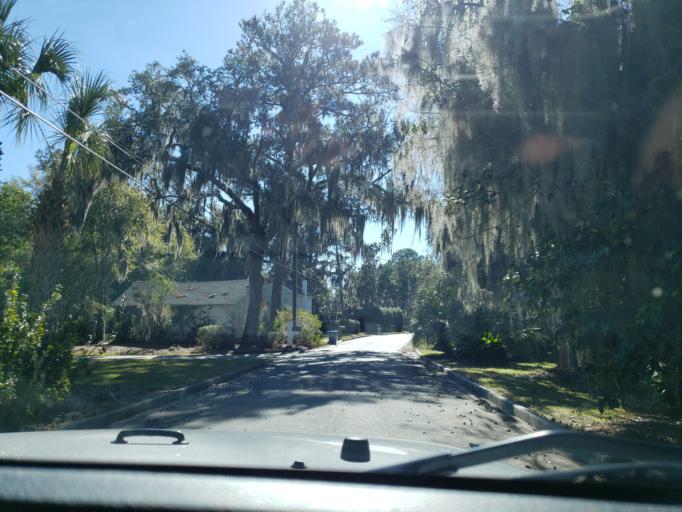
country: US
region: Georgia
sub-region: Chatham County
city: Whitemarsh Island
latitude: 32.0403
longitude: -80.9861
